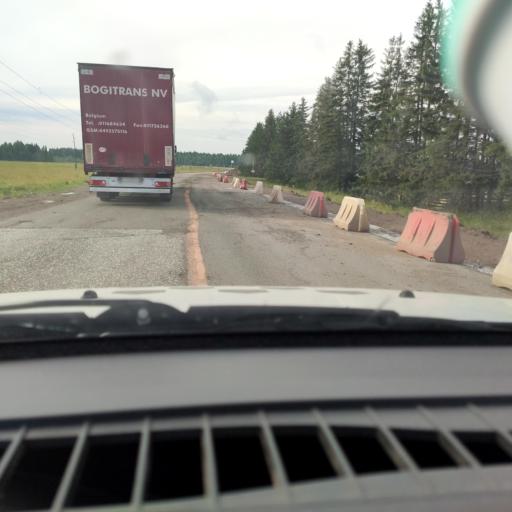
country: RU
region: Kirov
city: Kostino
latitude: 58.8269
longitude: 53.3099
